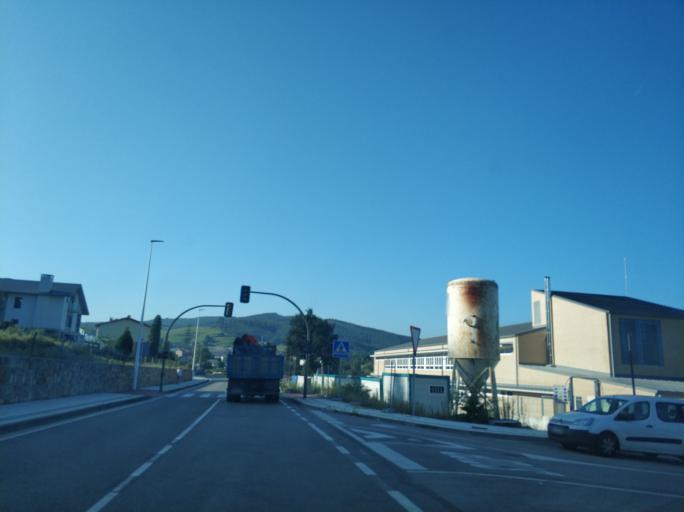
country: ES
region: Cantabria
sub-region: Provincia de Cantabria
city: Polanco
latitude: 43.3621
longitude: -3.9571
